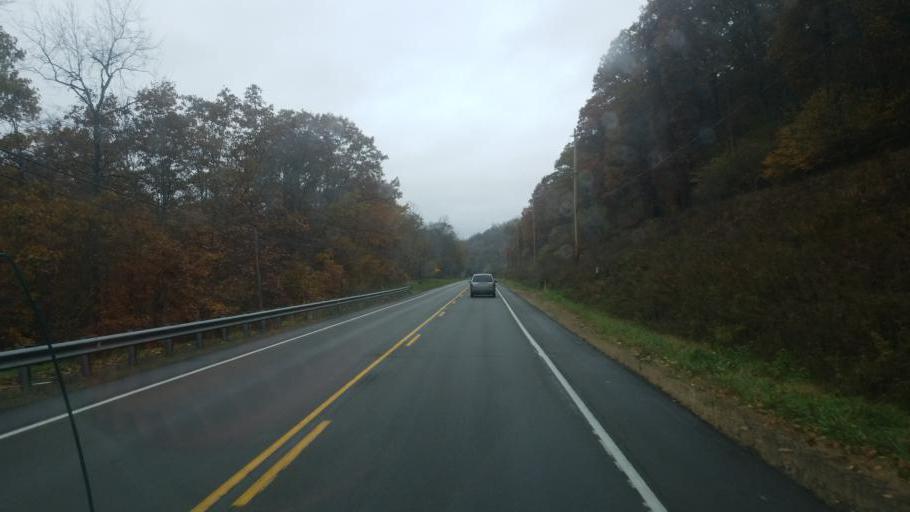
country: US
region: Pennsylvania
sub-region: Cameron County
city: Emporium
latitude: 41.4715
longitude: -78.3417
